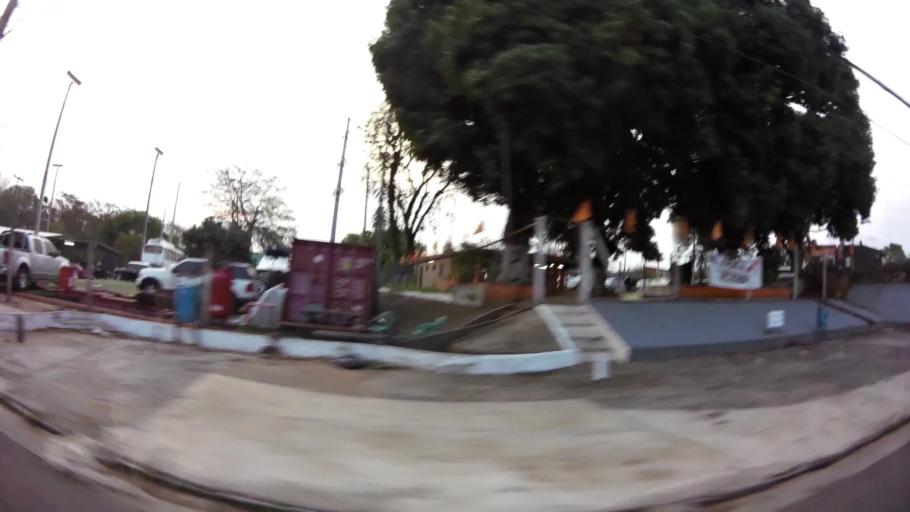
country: PY
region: Central
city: Lambare
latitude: -25.3397
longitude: -57.6234
